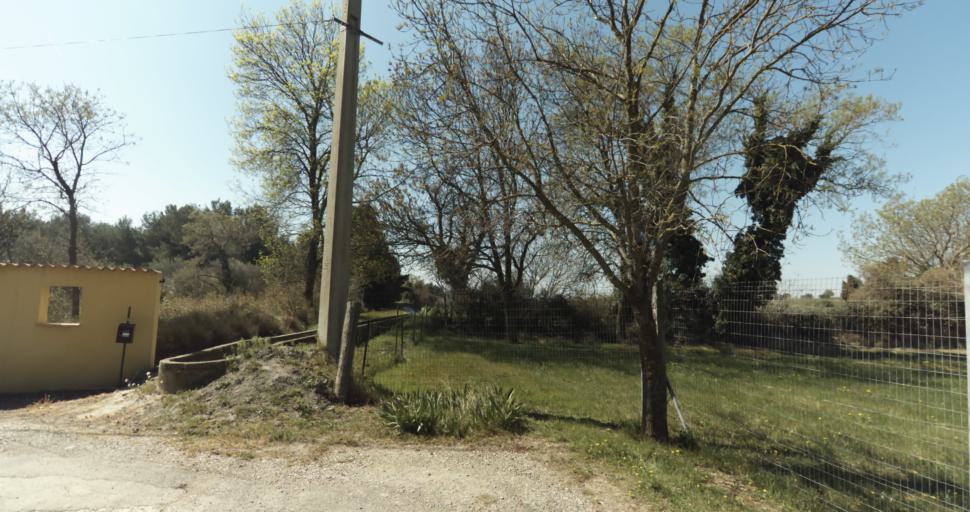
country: FR
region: Provence-Alpes-Cote d'Azur
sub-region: Departement des Bouches-du-Rhone
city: Pelissanne
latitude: 43.6158
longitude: 5.1452
